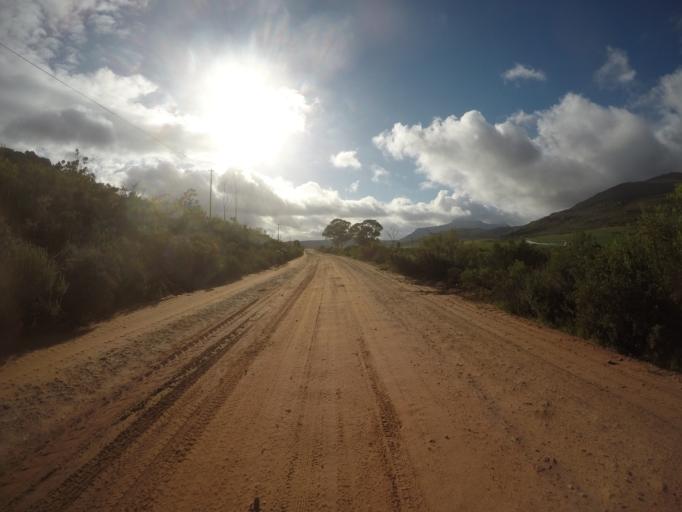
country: ZA
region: Western Cape
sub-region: West Coast District Municipality
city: Clanwilliam
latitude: -32.3436
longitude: 18.8188
